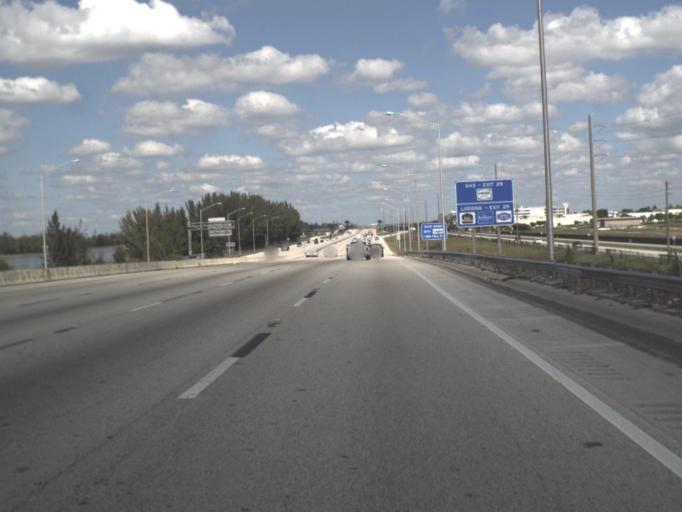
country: US
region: Florida
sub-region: Miami-Dade County
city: Sweetwater
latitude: 25.7978
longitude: -80.3858
